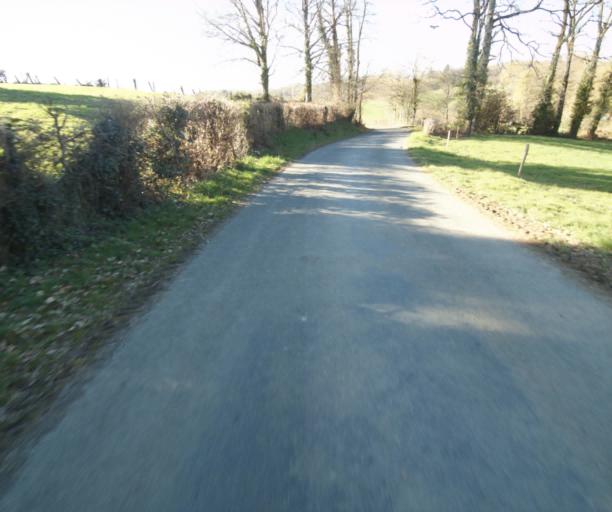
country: FR
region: Limousin
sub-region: Departement de la Correze
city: Seilhac
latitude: 45.3801
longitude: 1.7111
